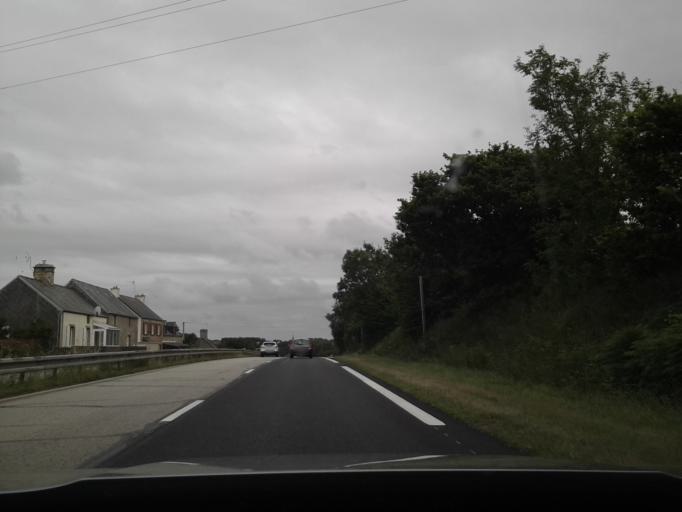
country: FR
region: Lower Normandy
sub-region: Departement de la Manche
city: Brix
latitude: 49.5431
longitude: -1.5504
